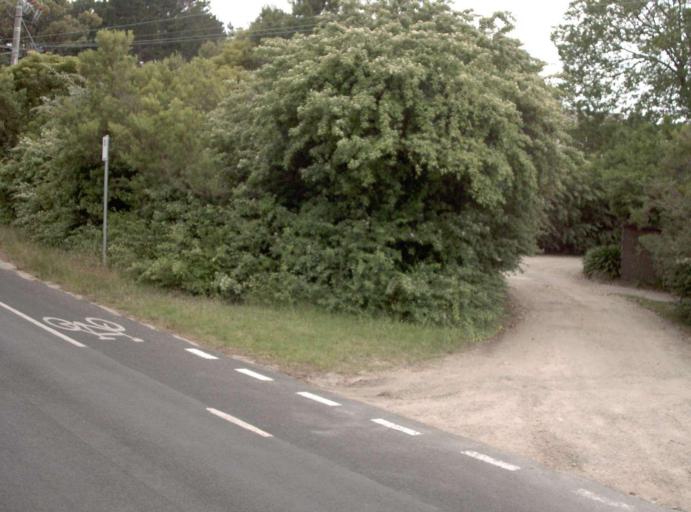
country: AU
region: Victoria
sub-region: Mornington Peninsula
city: Sorrento
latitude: -38.3294
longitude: 144.7373
